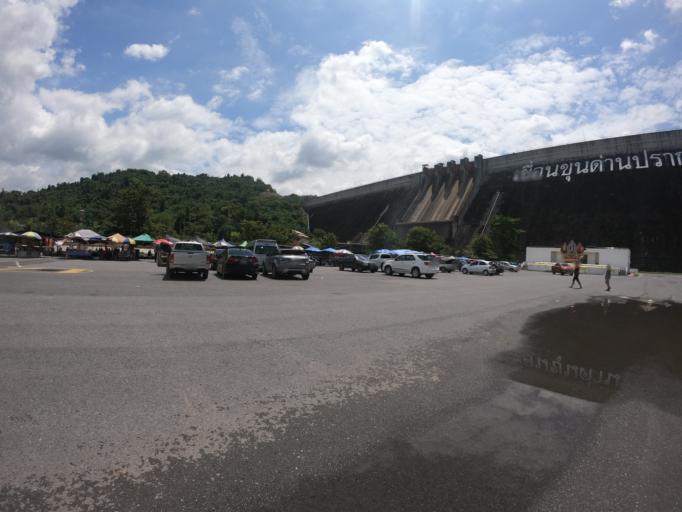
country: TH
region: Nakhon Nayok
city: Nakhon Nayok
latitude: 14.3108
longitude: 101.3191
